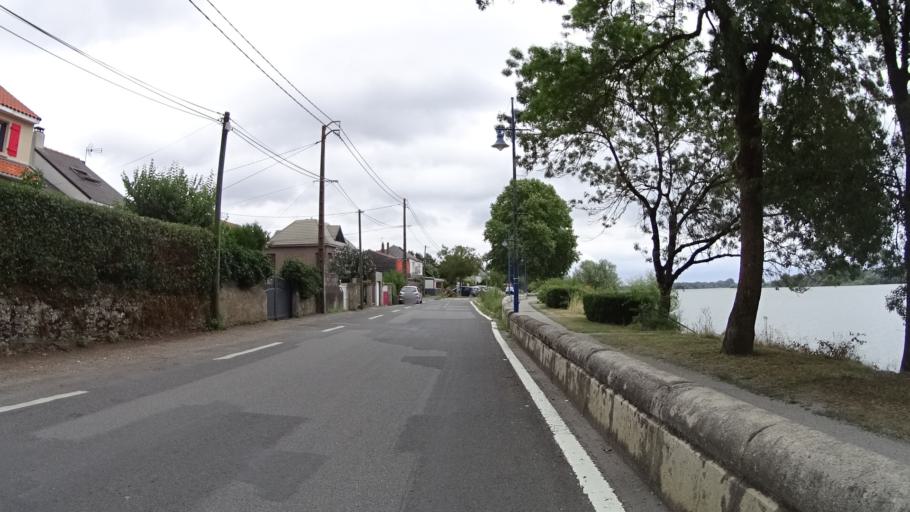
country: FR
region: Pays de la Loire
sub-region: Departement de la Loire-Atlantique
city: Sainte-Luce-sur-Loire
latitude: 47.2364
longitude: -1.4726
